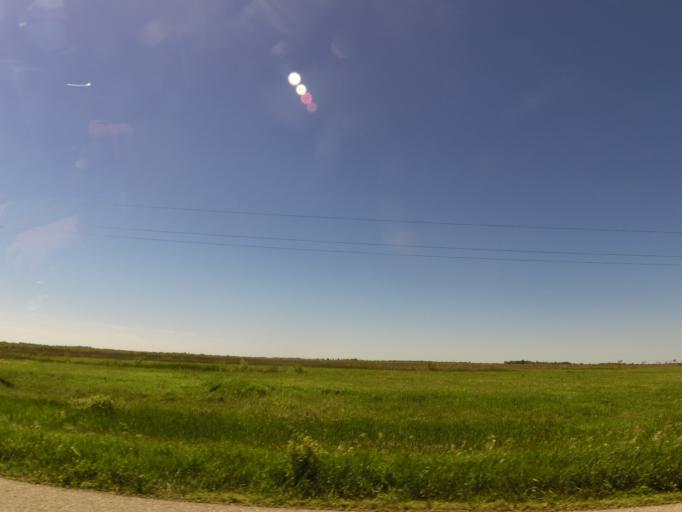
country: US
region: Minnesota
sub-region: Red Lake County
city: Red Lake Falls
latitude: 47.7603
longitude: -96.3666
